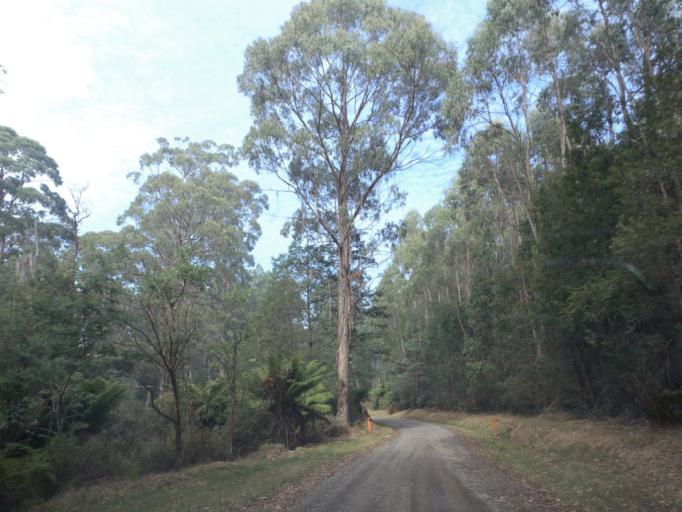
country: AU
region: Victoria
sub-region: Yarra Ranges
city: Healesville
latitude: -37.5621
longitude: 145.5416
